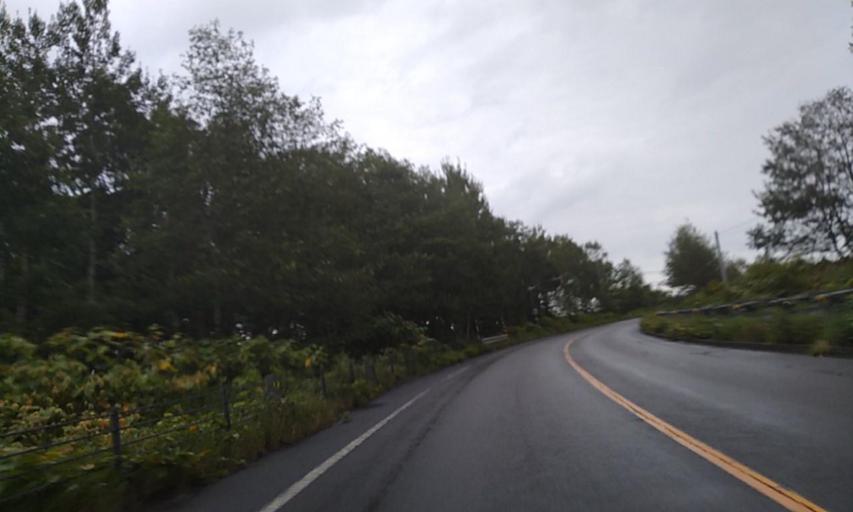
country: JP
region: Hokkaido
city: Mombetsu
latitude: 44.4885
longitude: 143.0924
